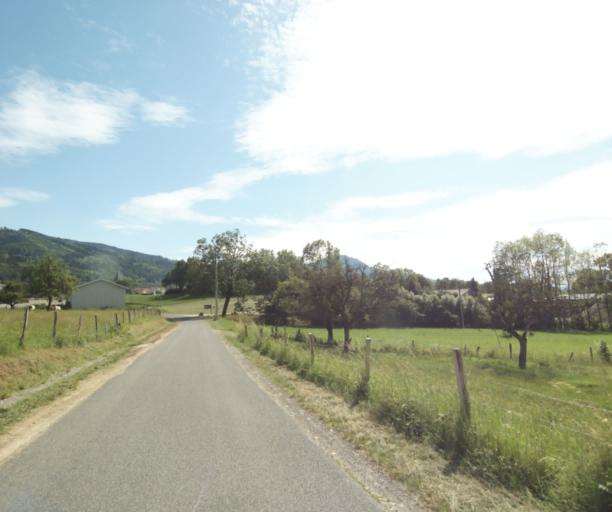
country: FR
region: Rhone-Alpes
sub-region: Departement de la Haute-Savoie
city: Bons-en-Chablais
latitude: 46.2802
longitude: 6.4133
